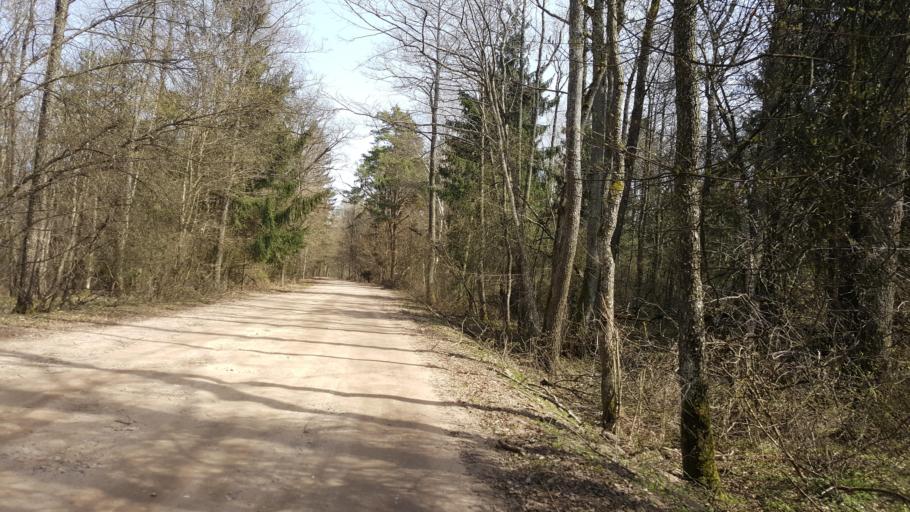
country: BY
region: Brest
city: Kamyanyuki
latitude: 52.5496
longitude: 23.6608
